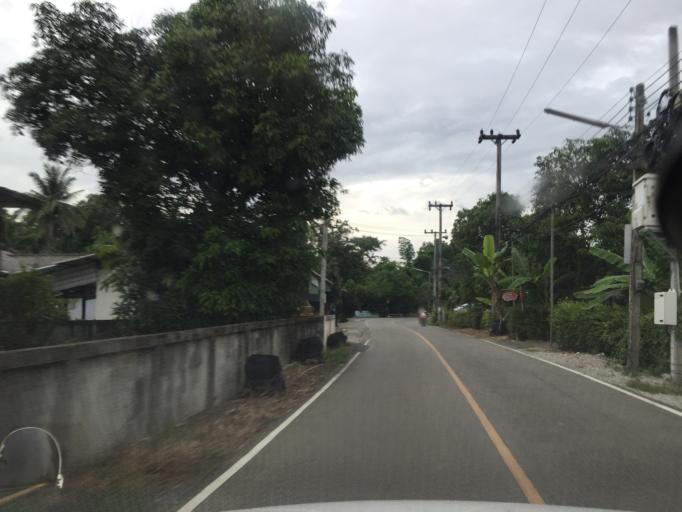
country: TH
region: Chiang Mai
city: Mae On
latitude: 18.8281
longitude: 99.1806
